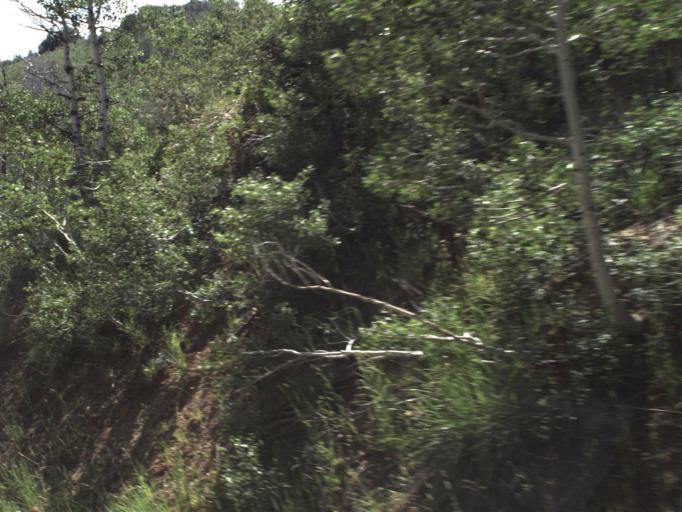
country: US
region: Utah
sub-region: Weber County
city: Wolf Creek
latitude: 41.4028
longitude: -111.5986
